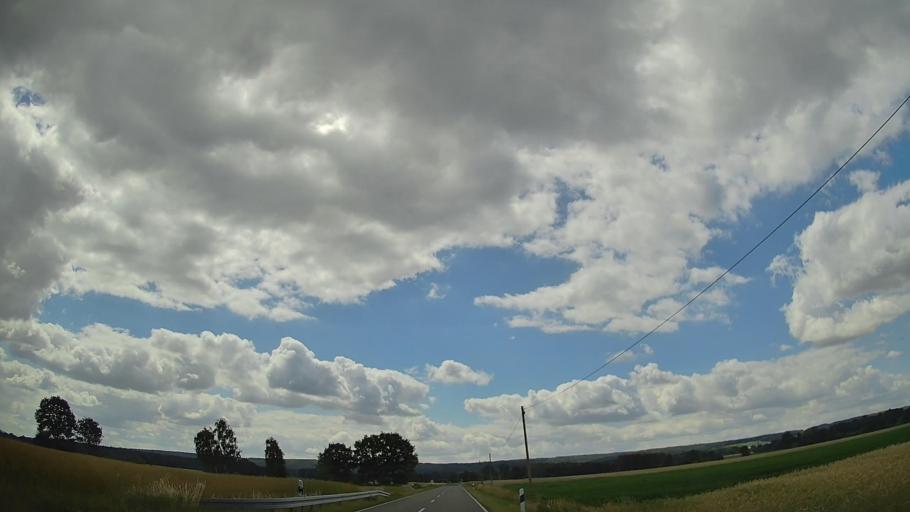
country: DE
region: Lower Saxony
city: Brockum
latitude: 52.4839
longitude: 8.4292
